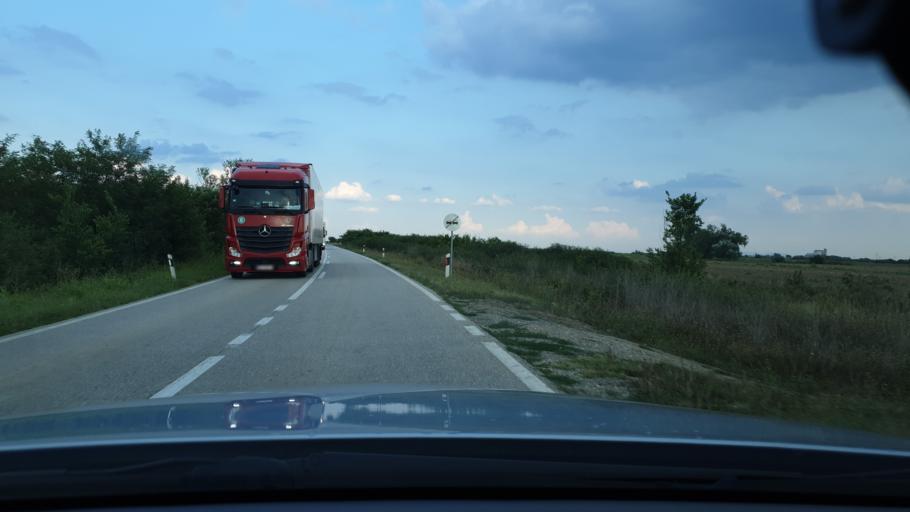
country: RS
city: Konak
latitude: 45.3293
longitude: 20.8816
